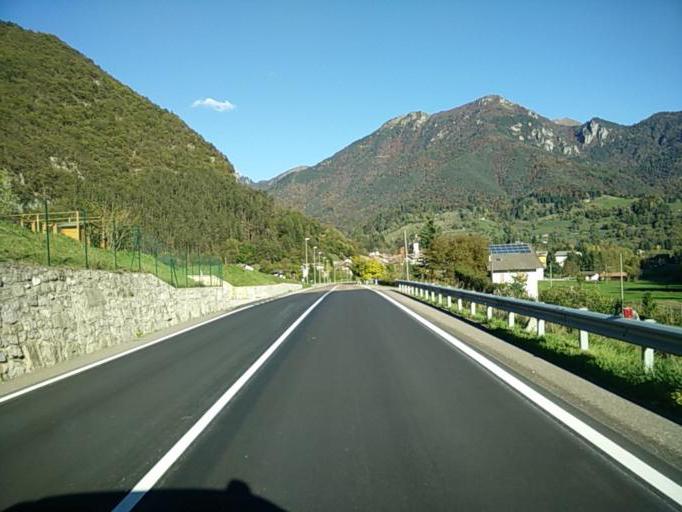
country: IT
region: Trentino-Alto Adige
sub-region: Provincia di Trento
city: Pieve di Ledro
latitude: 45.8938
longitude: 10.7097
